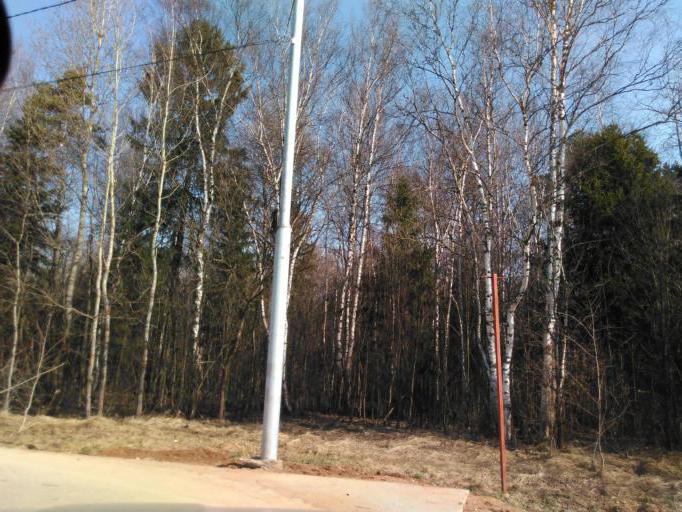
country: RU
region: Moskovskaya
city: Opalikha
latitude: 55.8738
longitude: 37.2614
